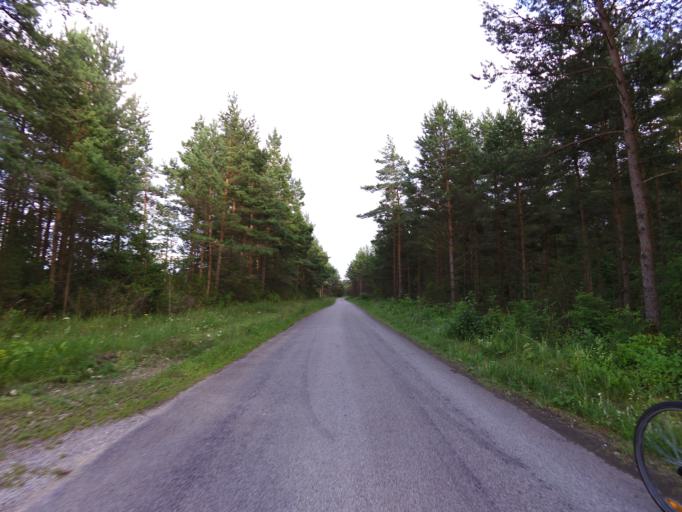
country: EE
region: Laeaene
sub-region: Vormsi vald
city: Hullo
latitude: 58.9795
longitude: 23.2533
